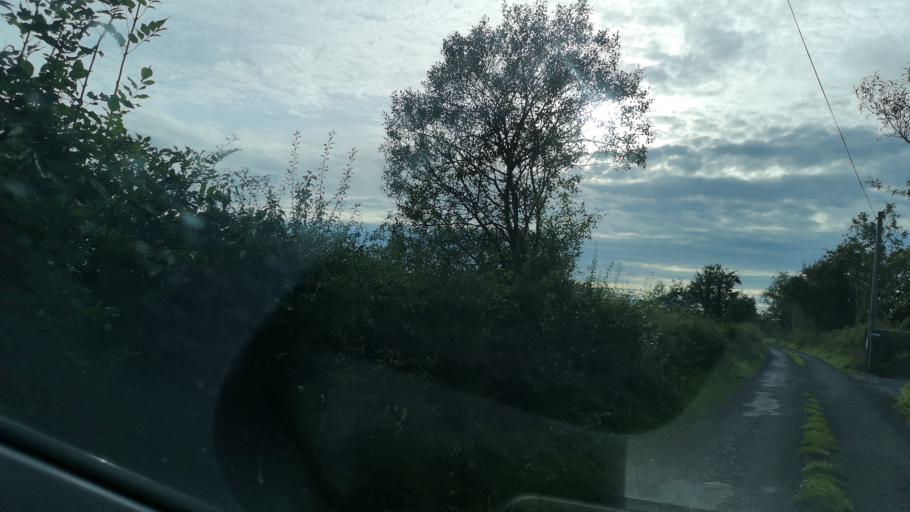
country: IE
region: Connaught
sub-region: County Galway
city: Ballinasloe
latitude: 53.3431
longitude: -8.2875
